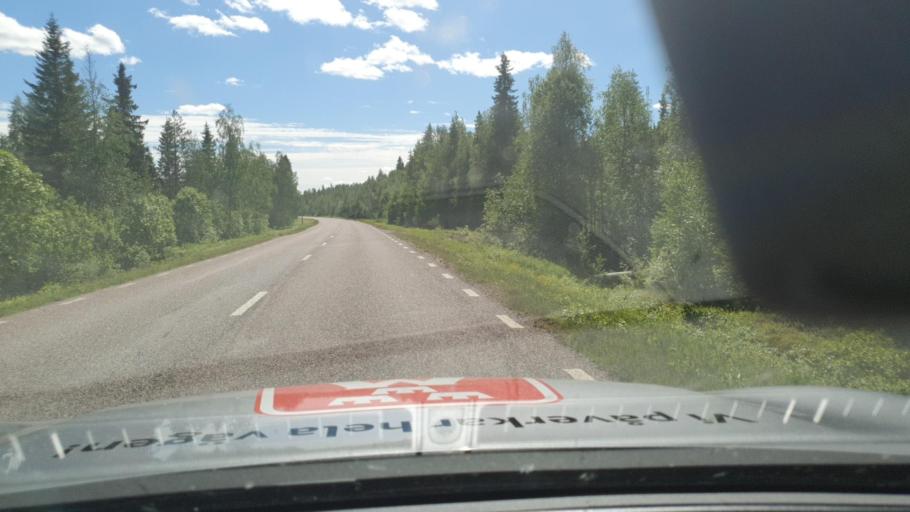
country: FI
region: Lapland
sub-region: Tunturi-Lappi
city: Kolari
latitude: 67.0763
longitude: 23.6604
